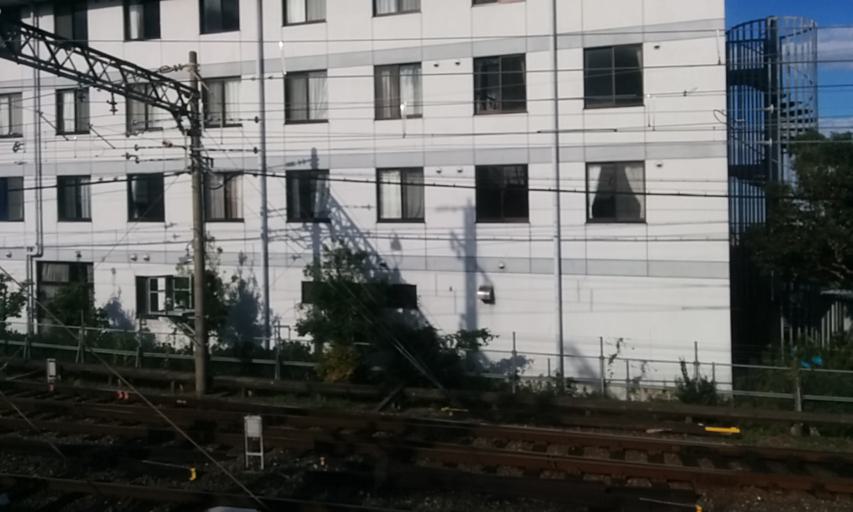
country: JP
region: Kyoto
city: Tanabe
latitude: 34.8250
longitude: 135.7735
